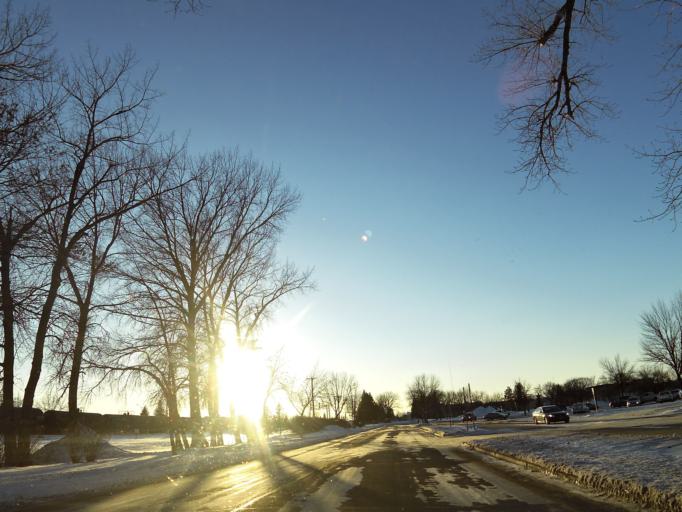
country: US
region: North Dakota
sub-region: Grand Forks County
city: Grand Forks
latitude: 47.9190
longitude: -97.0777
